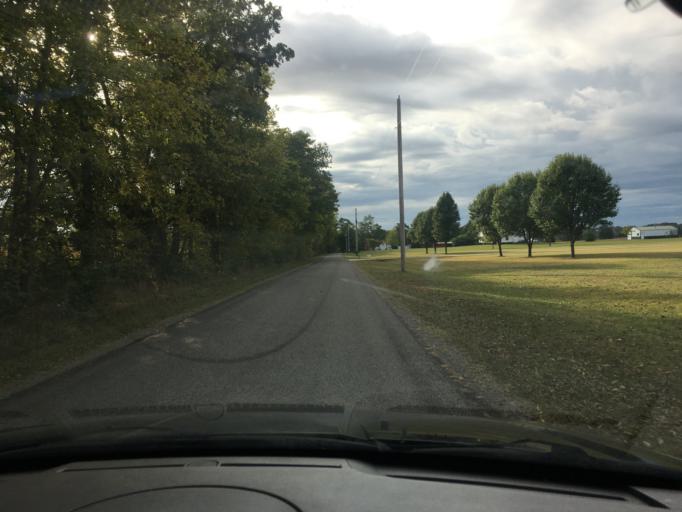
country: US
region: Ohio
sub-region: Logan County
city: West Liberty
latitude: 40.2568
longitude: -83.7331
